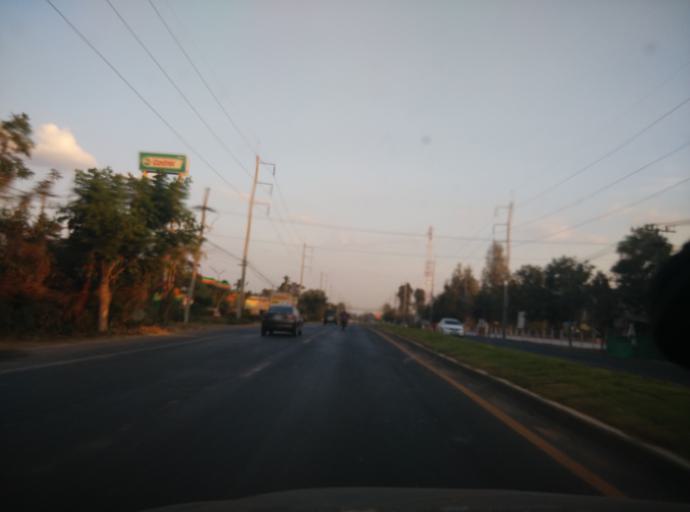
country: TH
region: Sisaket
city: Si Sa Ket
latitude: 15.1308
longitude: 104.2758
